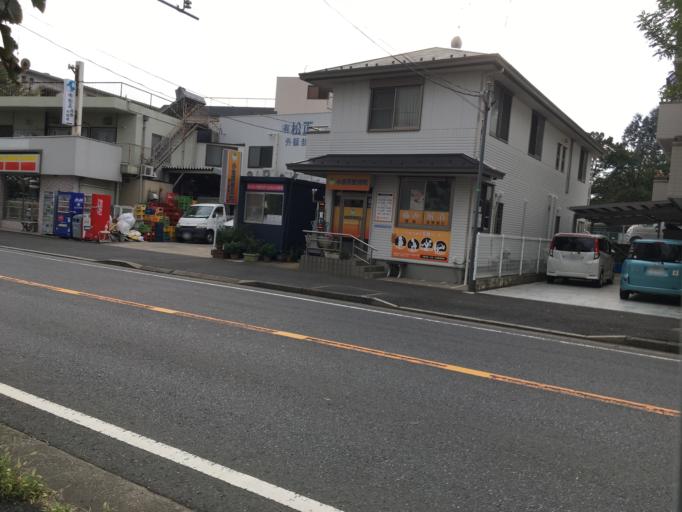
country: JP
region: Chiba
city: Kashiwa
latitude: 35.8195
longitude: 139.9493
